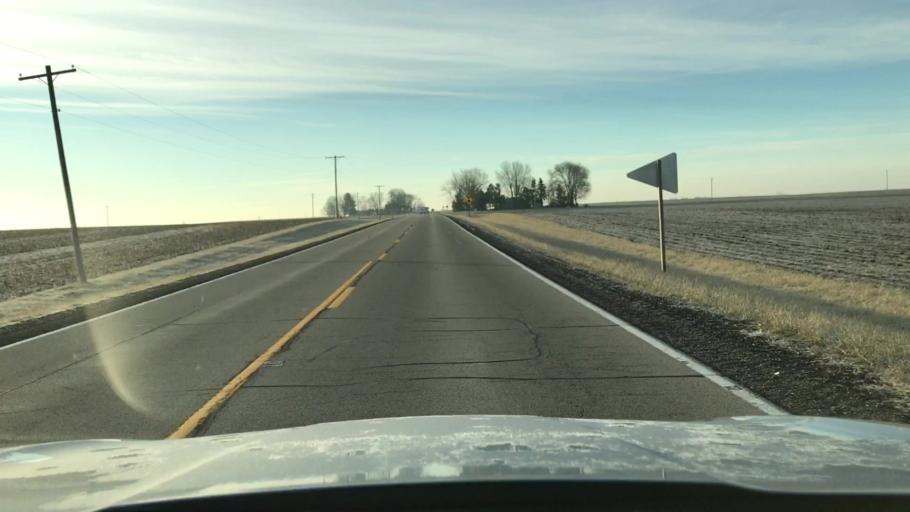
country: US
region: Illinois
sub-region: McLean County
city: Hudson
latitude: 40.6088
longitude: -88.9452
